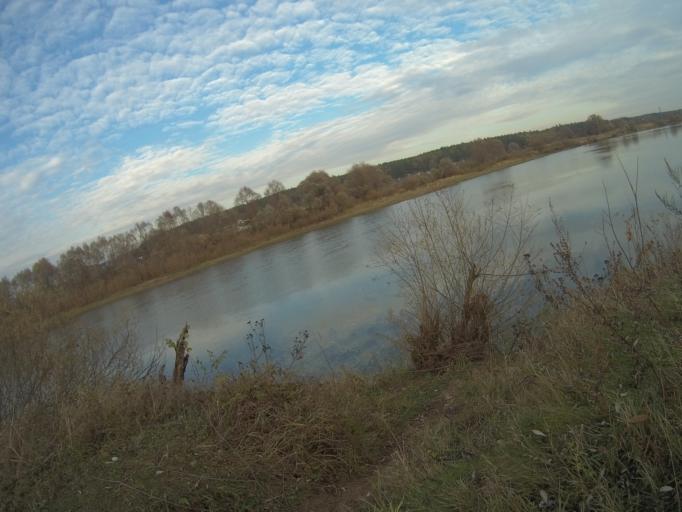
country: RU
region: Vladimir
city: Orgtrud
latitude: 56.1693
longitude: 40.6147
